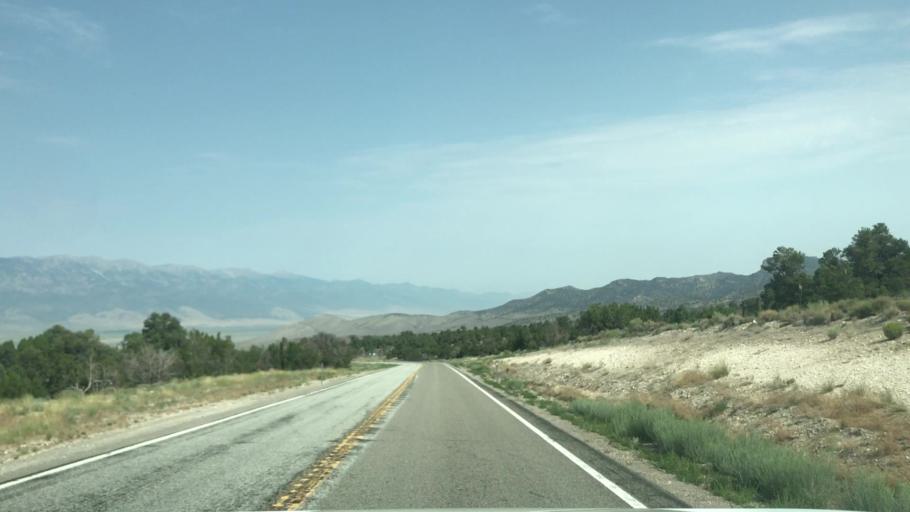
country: US
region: Nevada
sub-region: White Pine County
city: McGill
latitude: 39.1546
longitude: -114.3479
